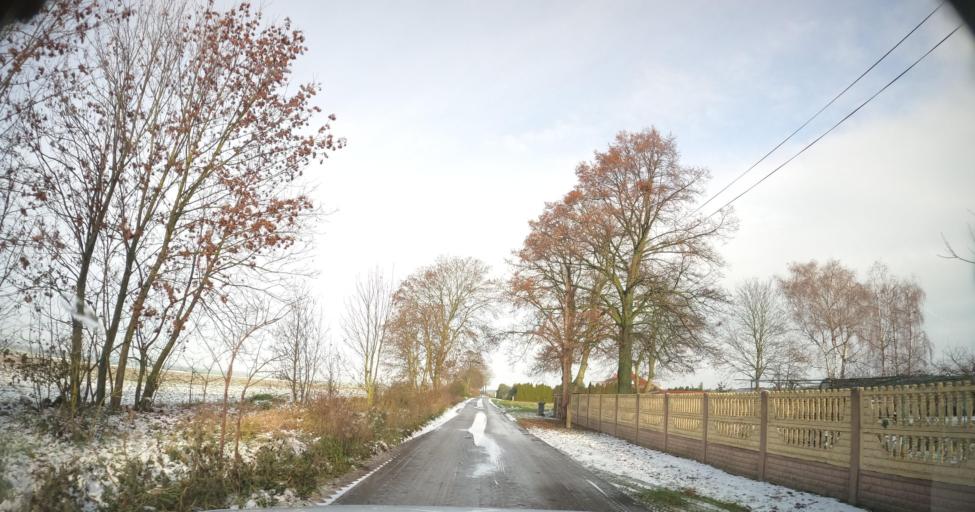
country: PL
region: West Pomeranian Voivodeship
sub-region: Powiat gryfinski
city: Mieszkowice
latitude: 52.7415
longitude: 14.4910
